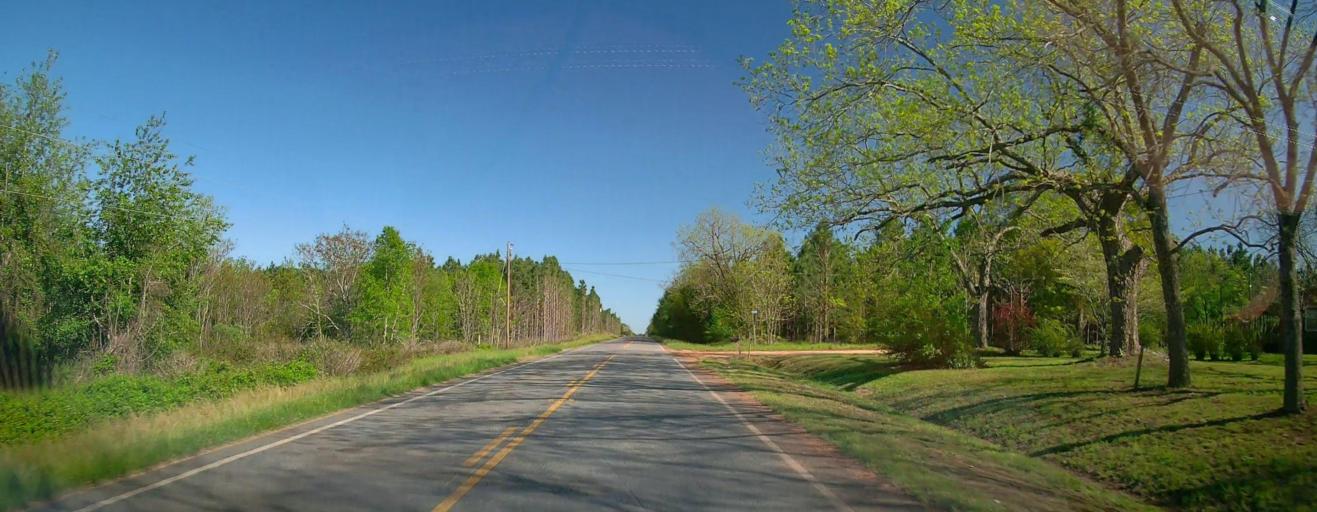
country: US
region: Georgia
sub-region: Wilcox County
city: Rochelle
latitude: 31.9983
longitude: -83.4767
